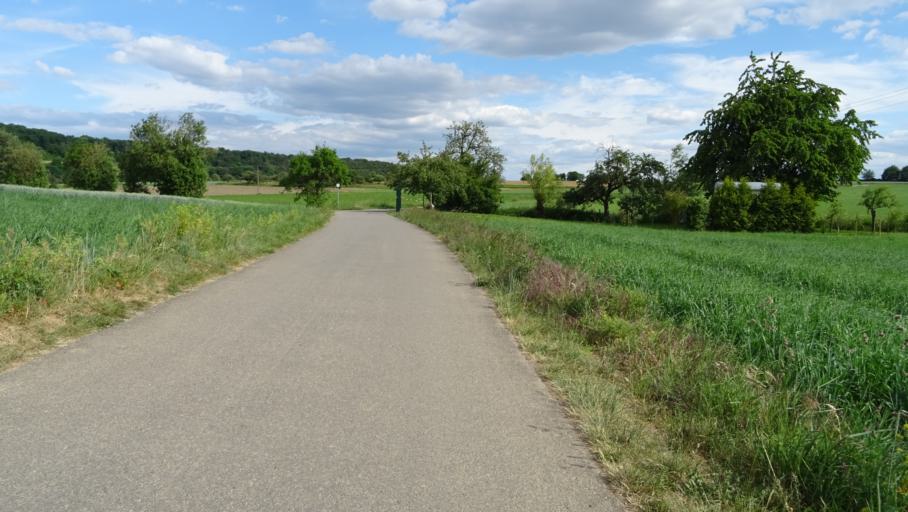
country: DE
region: Baden-Wuerttemberg
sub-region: Regierungsbezirk Stuttgart
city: Gundelsheim
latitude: 49.2750
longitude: 9.1641
